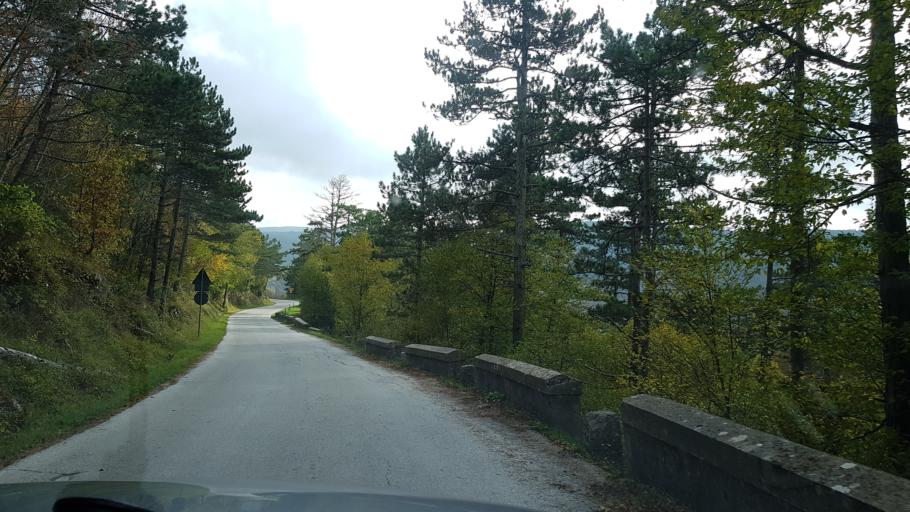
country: HR
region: Istarska
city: Buzet
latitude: 45.4108
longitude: 14.1156
